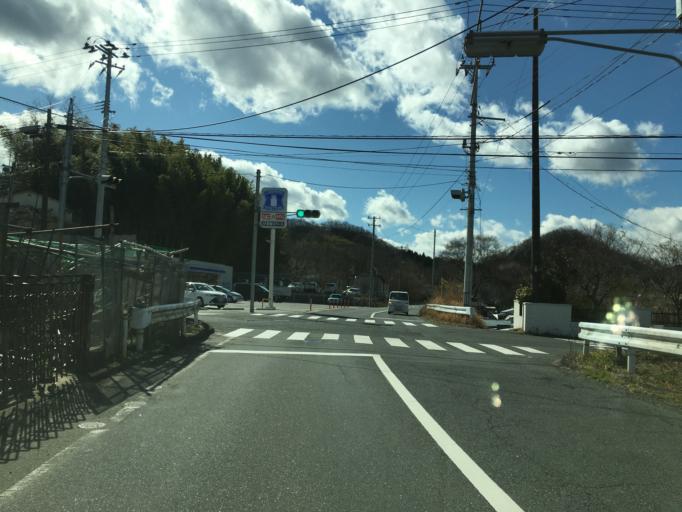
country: JP
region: Fukushima
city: Iwaki
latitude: 37.0116
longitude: 140.8347
